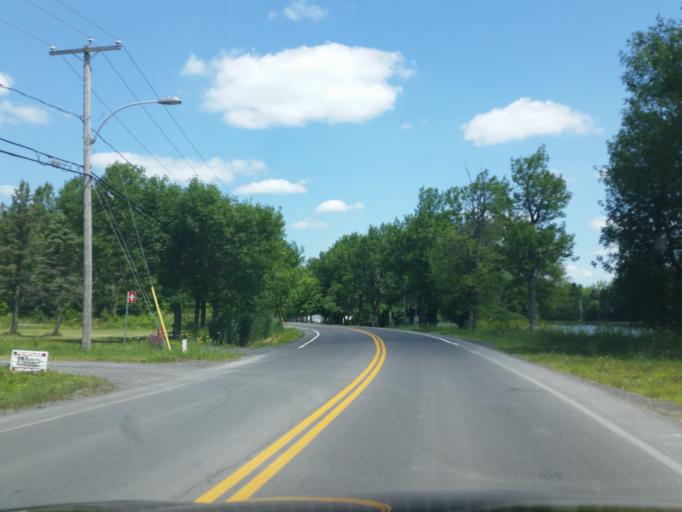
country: CA
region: Quebec
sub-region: Monteregie
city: Saint-Jean-sur-Richelieu
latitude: 45.3751
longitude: -73.2576
